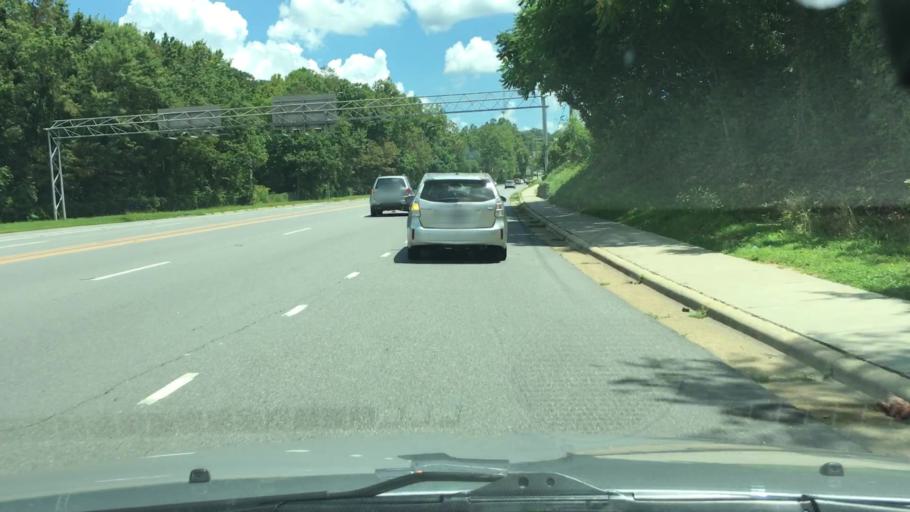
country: US
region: North Carolina
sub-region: Buncombe County
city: Asheville
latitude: 35.5863
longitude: -82.5173
